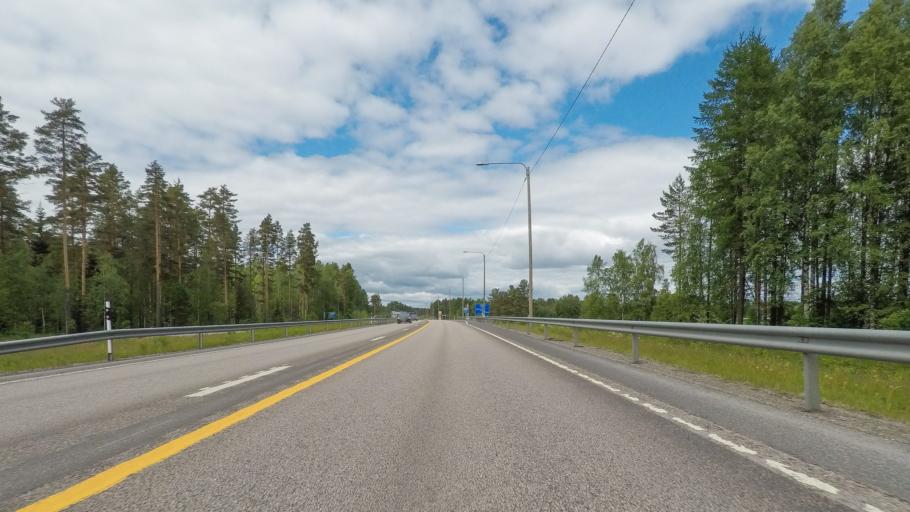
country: FI
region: Paijanne Tavastia
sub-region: Lahti
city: Hartola
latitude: 61.5598
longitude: 26.0059
